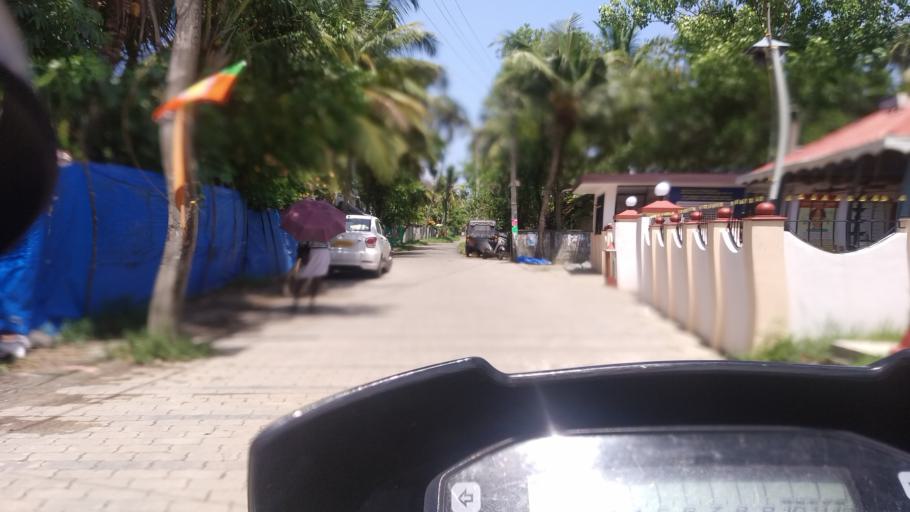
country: IN
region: Kerala
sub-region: Ernakulam
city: Elur
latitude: 10.0737
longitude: 76.2076
